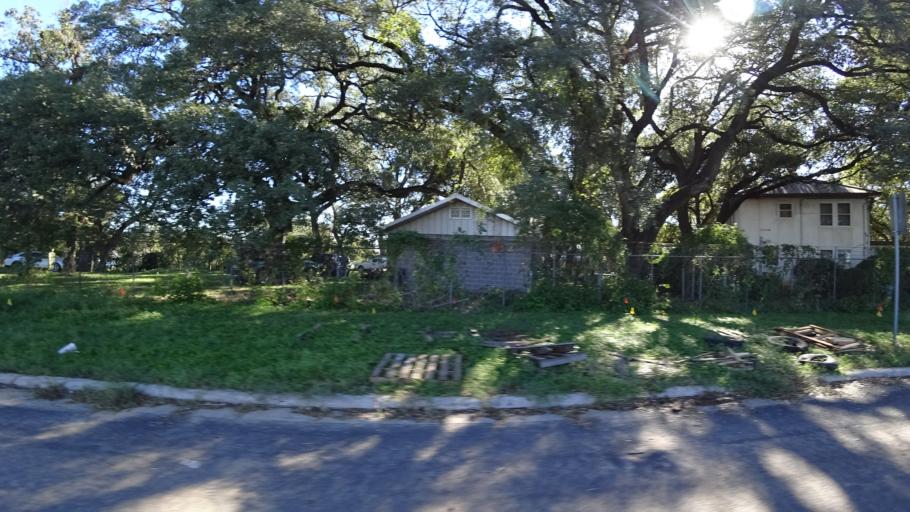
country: US
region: Texas
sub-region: Travis County
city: Austin
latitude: 30.2420
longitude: -97.6889
